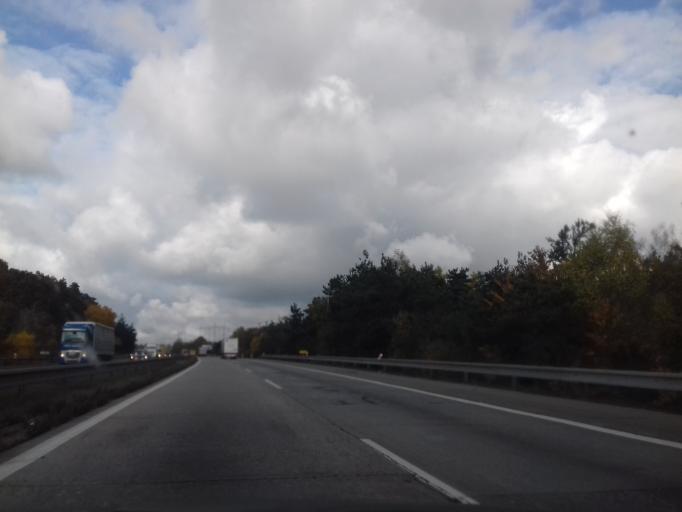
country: CZ
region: South Moravian
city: Ricany
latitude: 49.2416
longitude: 16.3691
